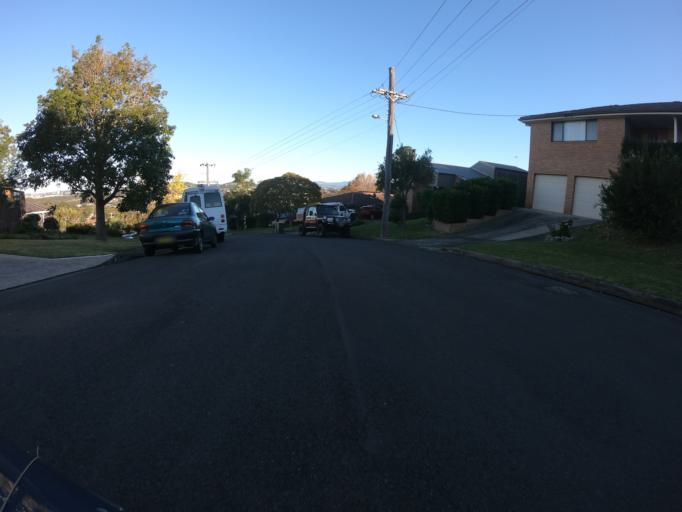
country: AU
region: New South Wales
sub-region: Wollongong
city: Mount Keira
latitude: -34.4278
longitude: 150.8437
